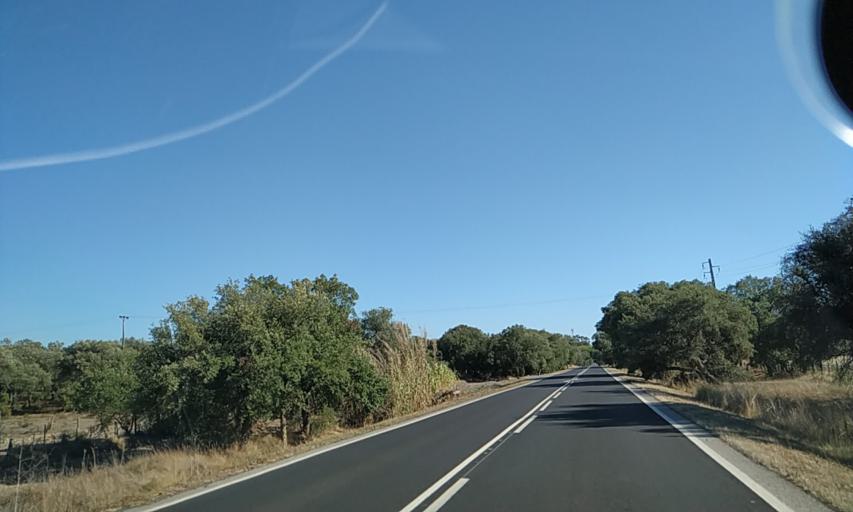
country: PT
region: Santarem
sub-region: Benavente
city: Poceirao
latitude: 38.8423
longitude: -8.8810
